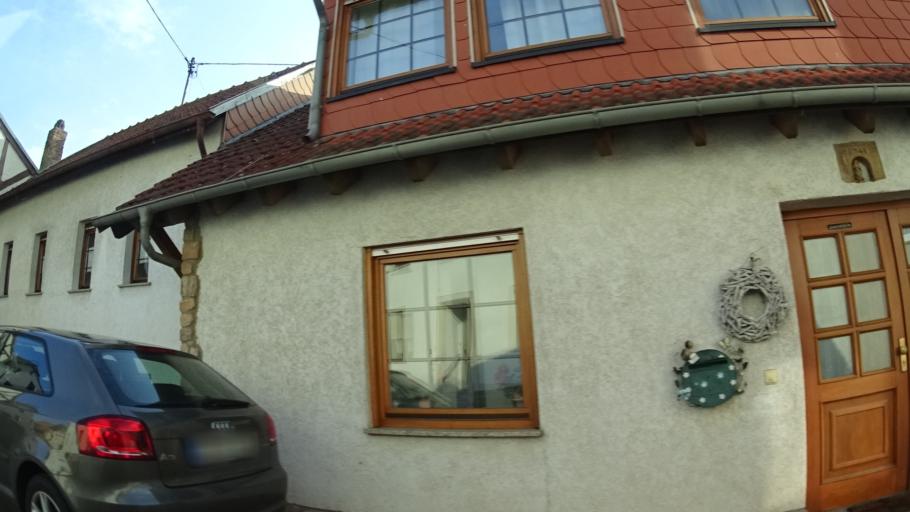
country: DE
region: Rheinland-Pfalz
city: Sponheim
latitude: 49.8439
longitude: 7.7254
